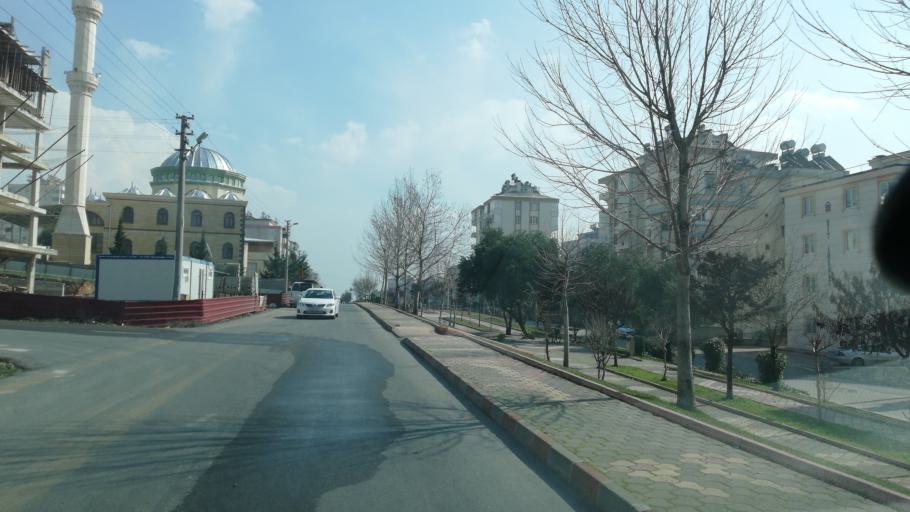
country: TR
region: Kahramanmaras
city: Kahramanmaras
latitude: 37.5891
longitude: 36.8916
